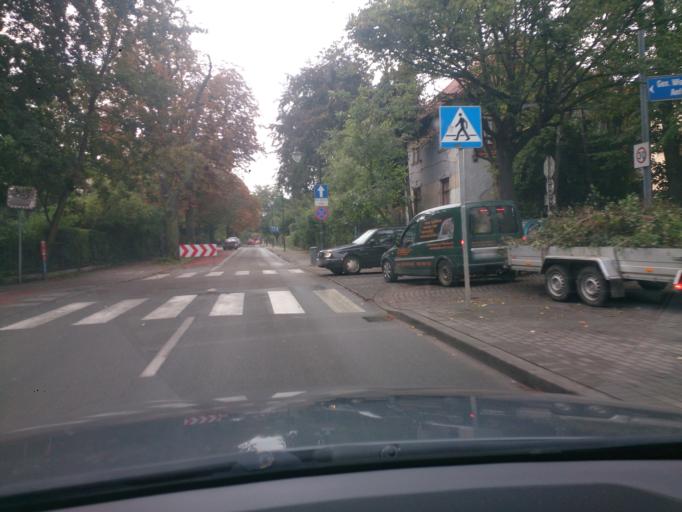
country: PL
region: Pomeranian Voivodeship
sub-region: Sopot
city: Sopot
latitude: 54.4409
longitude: 18.5568
